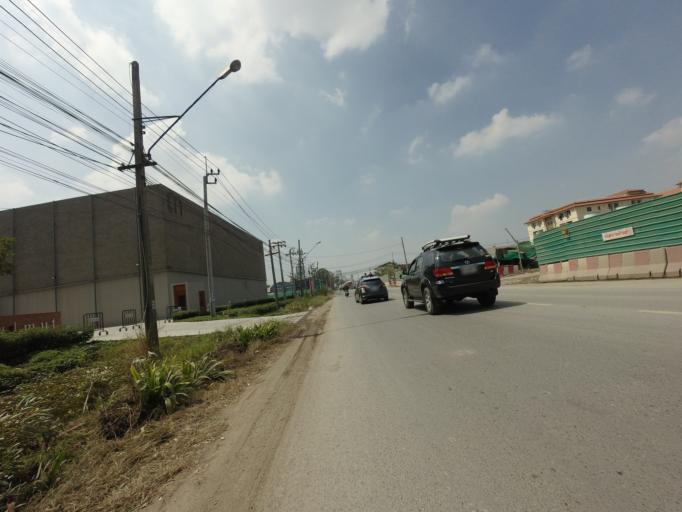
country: TH
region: Bangkok
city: Suan Luang
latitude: 13.7475
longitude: 100.6575
